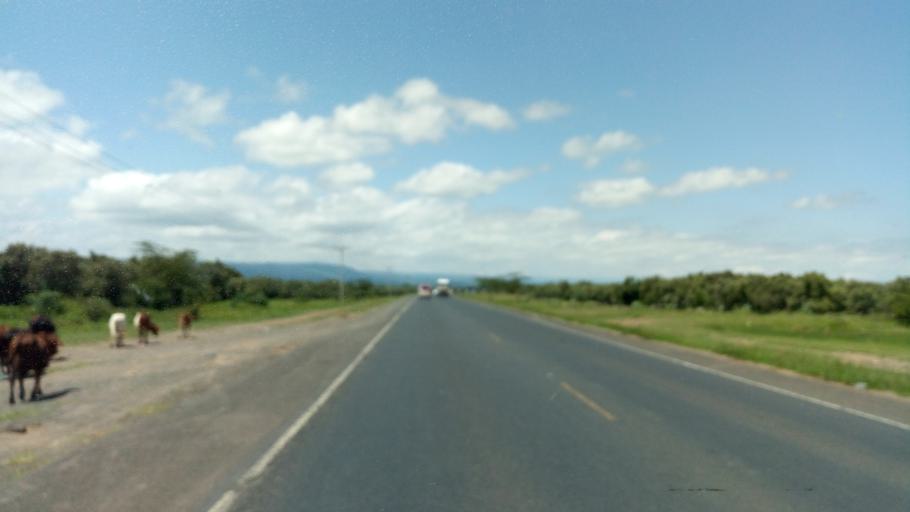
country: KE
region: Nakuru
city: Naivasha
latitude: -0.5452
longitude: 36.3423
